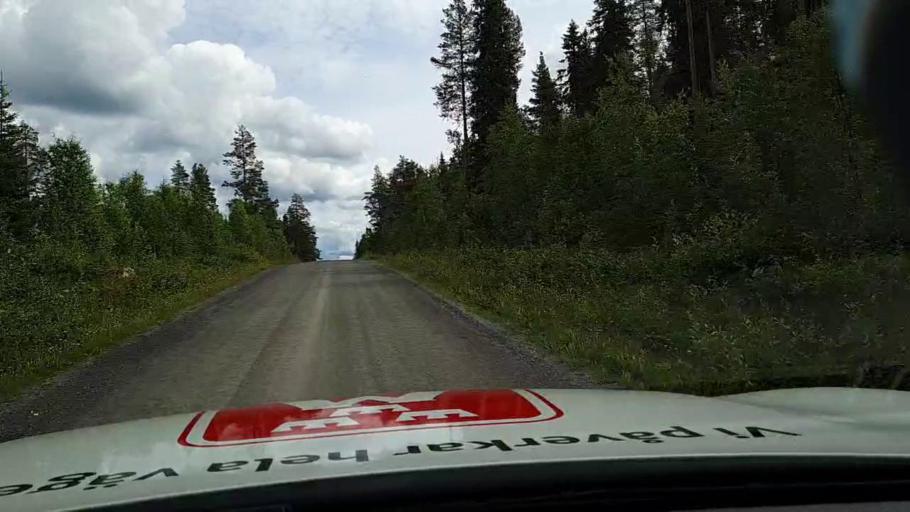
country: SE
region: Jaemtland
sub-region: OEstersunds Kommun
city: Lit
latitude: 63.2913
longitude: 15.3478
